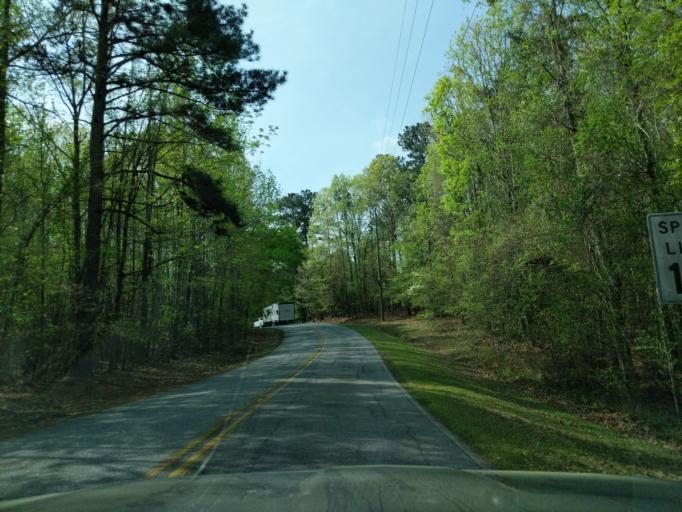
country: US
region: Georgia
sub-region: Lincoln County
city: Lincolnton
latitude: 33.8528
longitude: -82.4035
